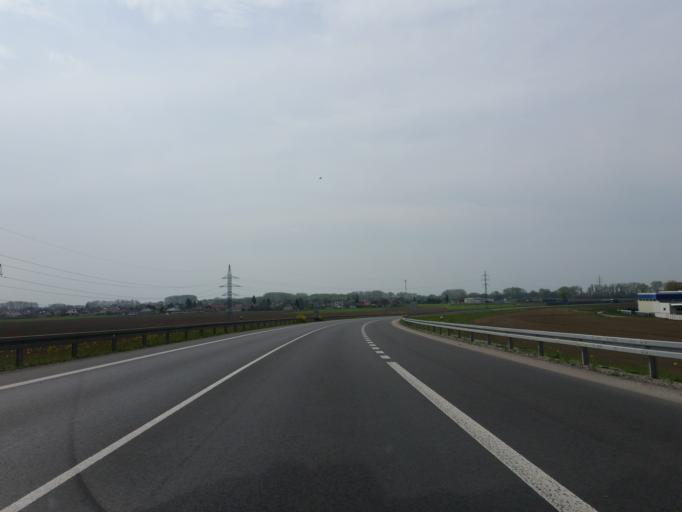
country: SK
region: Trnavsky
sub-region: Okres Galanta
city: Galanta
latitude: 48.1812
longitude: 17.7407
